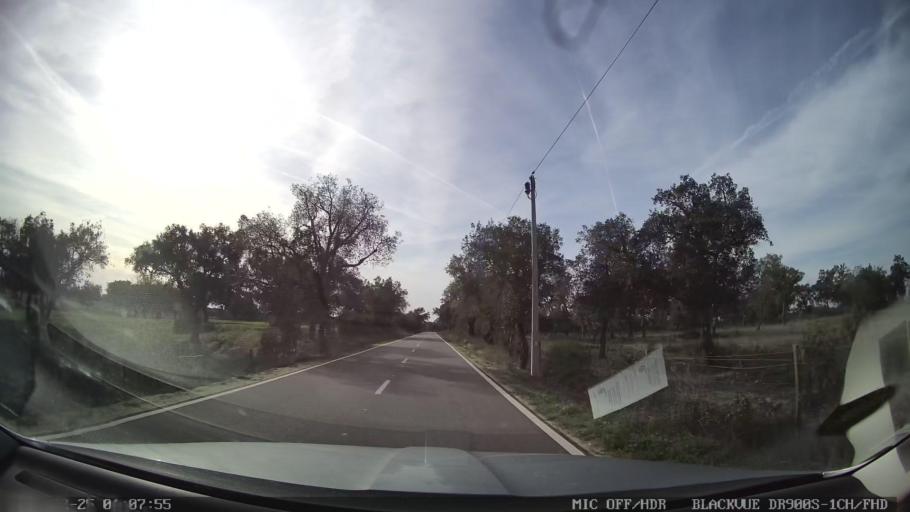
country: PT
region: Portalegre
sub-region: Nisa
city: Nisa
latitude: 39.4565
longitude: -7.7073
